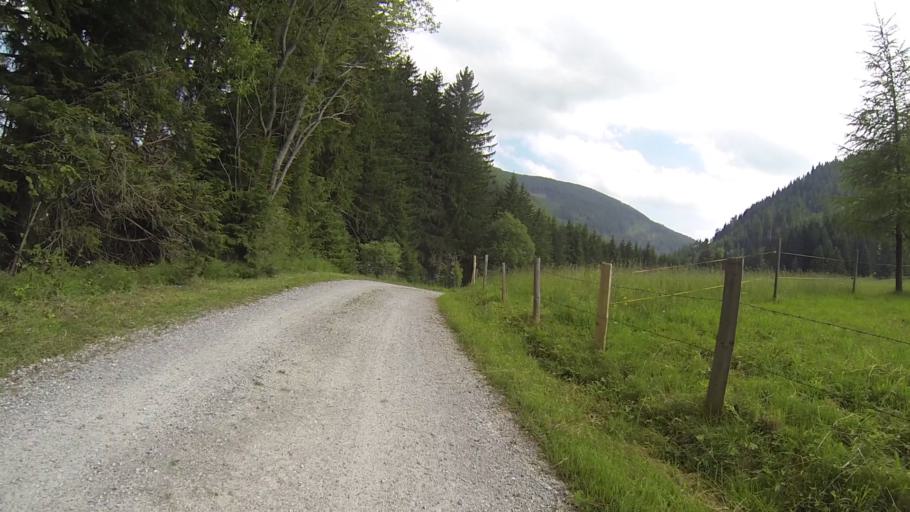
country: AT
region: Tyrol
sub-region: Politischer Bezirk Reutte
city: Jungholz
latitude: 47.6010
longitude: 10.4700
